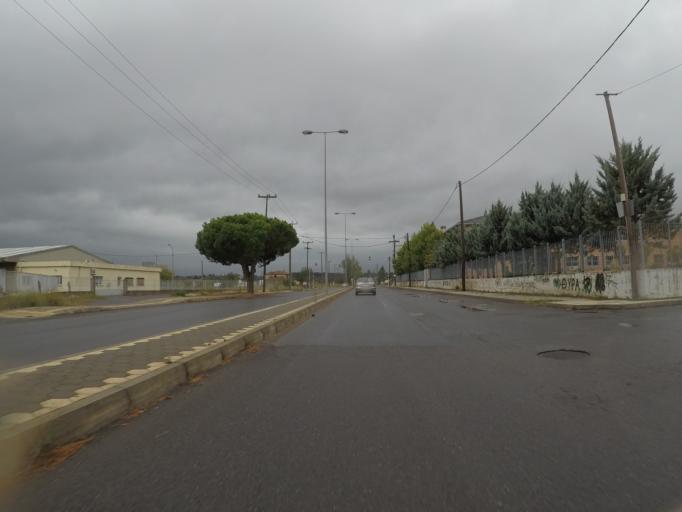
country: GR
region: Peloponnese
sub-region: Nomos Arkadias
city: Tripoli
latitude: 37.5012
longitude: 22.3777
